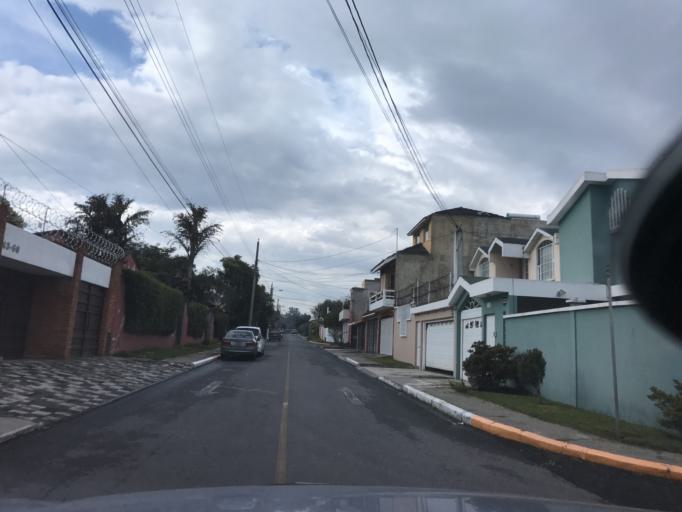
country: GT
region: Guatemala
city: Santa Catarina Pinula
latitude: 14.5780
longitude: -90.5530
